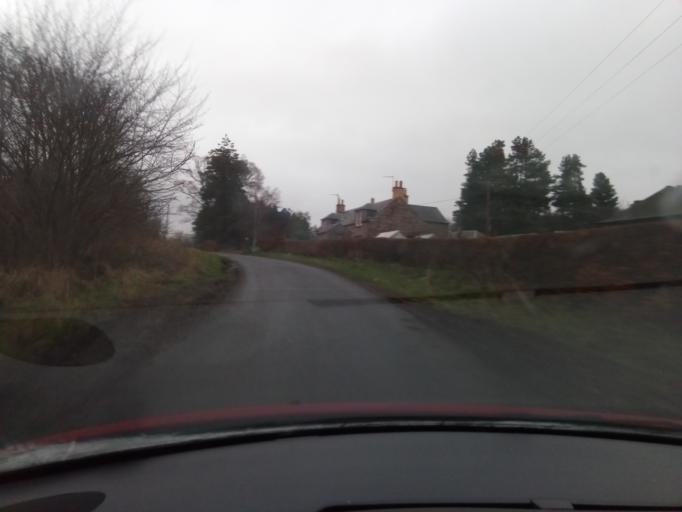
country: GB
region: Scotland
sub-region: The Scottish Borders
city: Kelso
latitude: 55.5514
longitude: -2.4316
